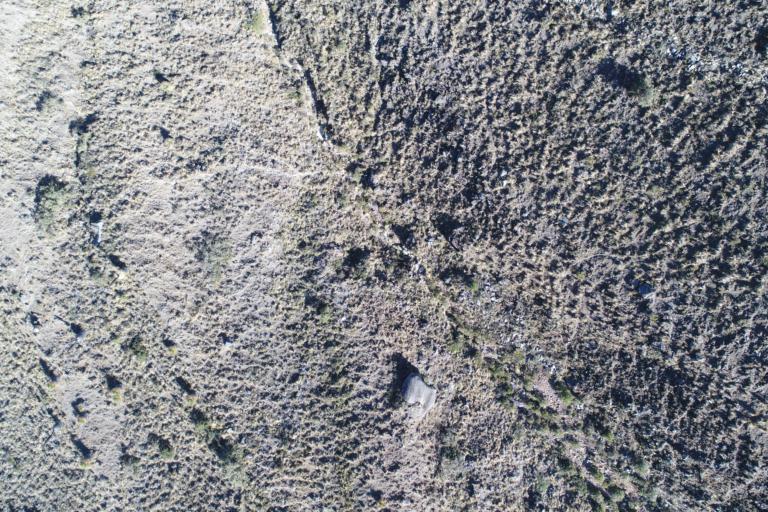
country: BO
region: La Paz
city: Viloco
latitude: -16.8084
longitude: -67.5546
